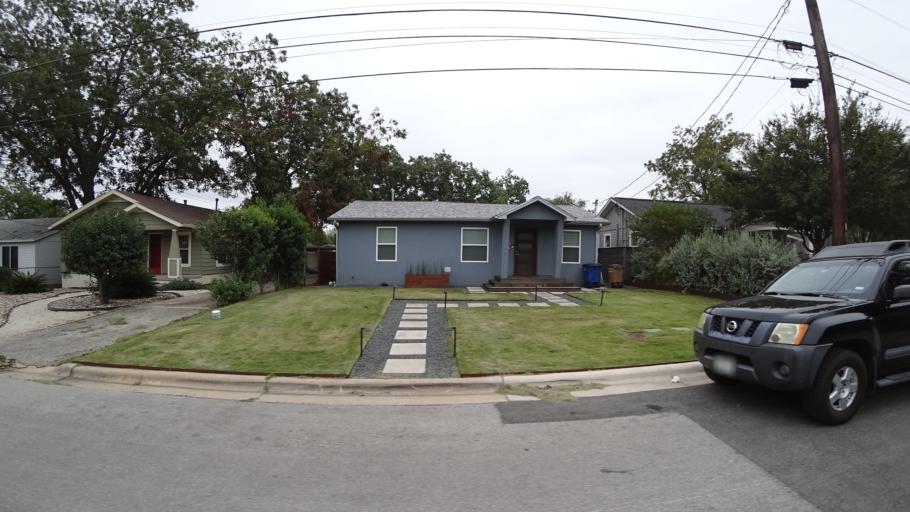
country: US
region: Texas
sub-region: Travis County
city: Austin
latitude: 30.2824
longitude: -97.7181
